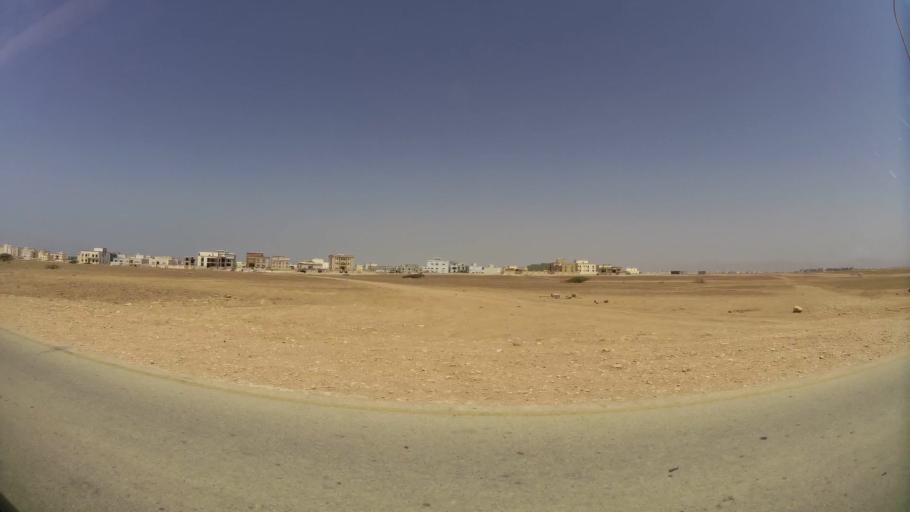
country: OM
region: Zufar
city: Salalah
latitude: 17.0543
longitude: 54.2106
